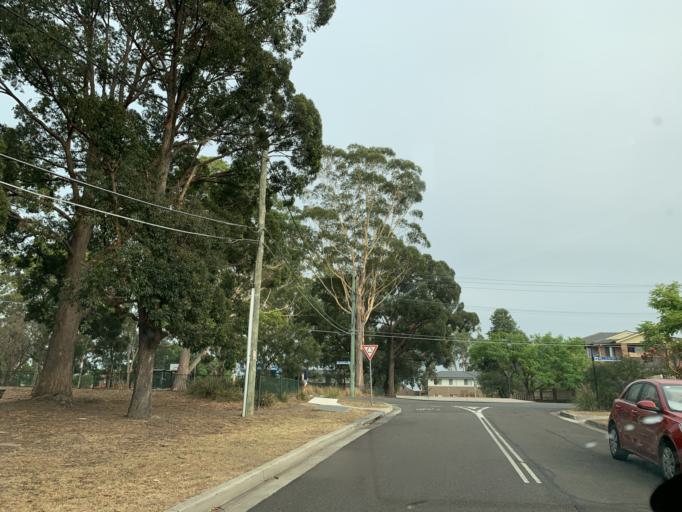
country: AU
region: New South Wales
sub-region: Parramatta
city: Dundas Valley
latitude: -33.7772
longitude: 151.0653
